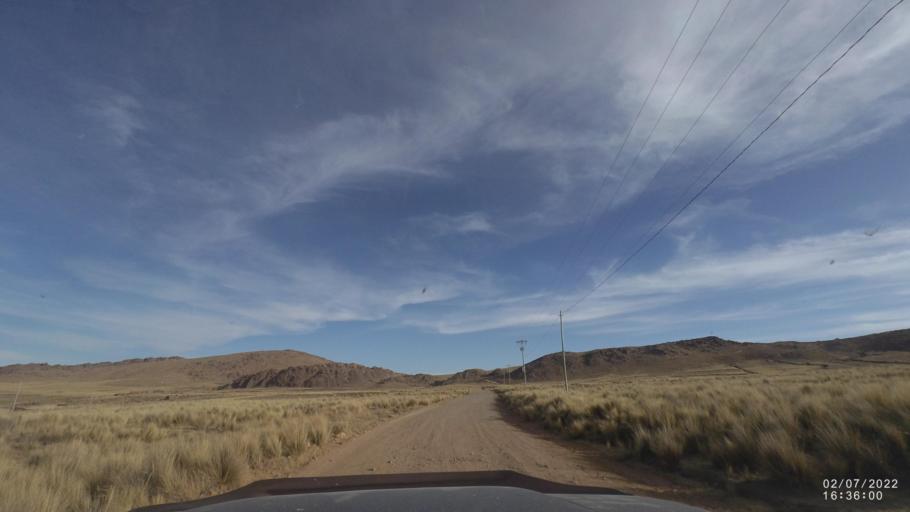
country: BO
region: Cochabamba
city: Irpa Irpa
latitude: -17.9591
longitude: -66.4937
